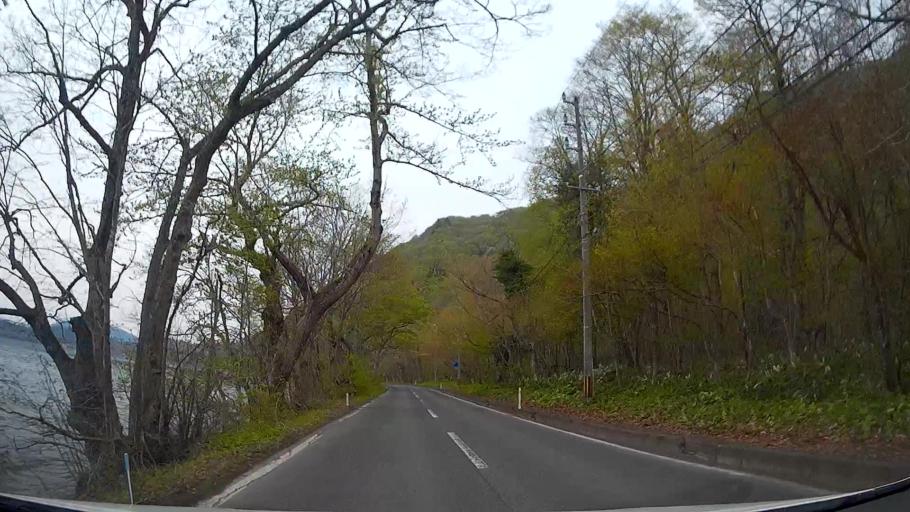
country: JP
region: Akita
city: Hanawa
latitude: 40.4152
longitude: 140.8853
